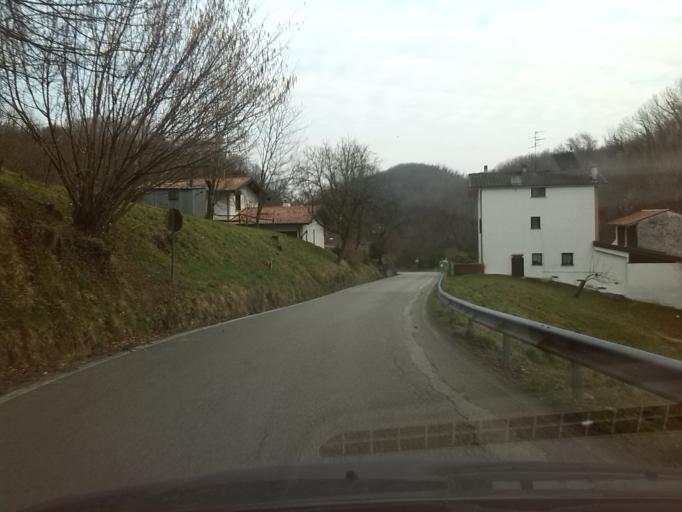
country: IT
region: Friuli Venezia Giulia
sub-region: Provincia di Gorizia
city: San Floriano del Collio
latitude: 45.9603
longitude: 13.5948
